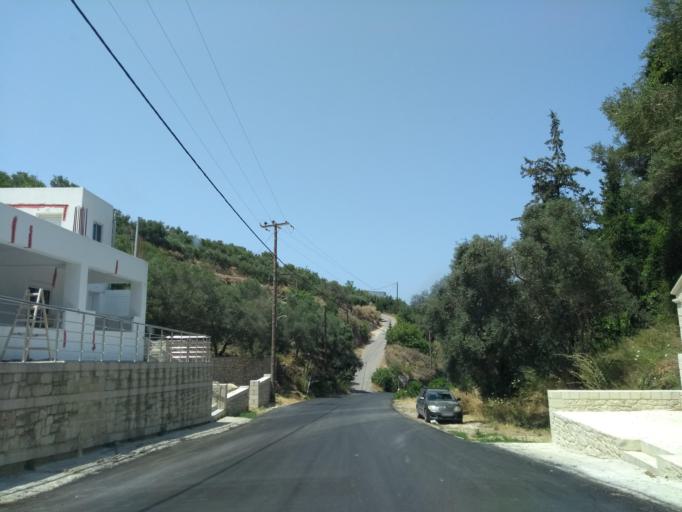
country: GR
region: Crete
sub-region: Nomos Chanias
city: Georgioupolis
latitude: 35.3166
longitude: 24.2986
